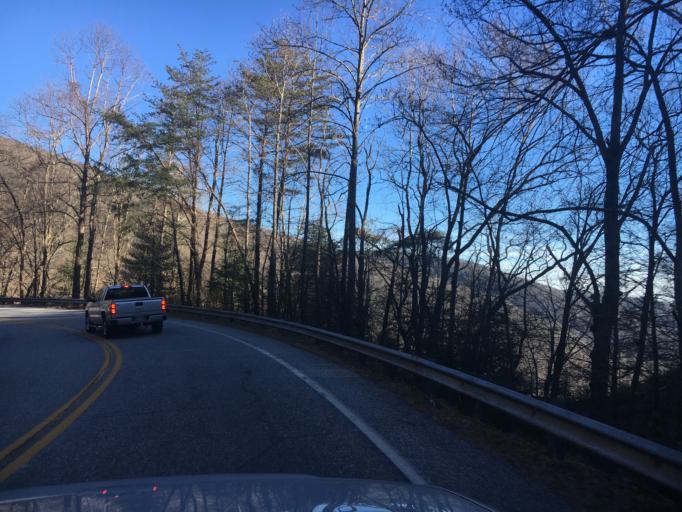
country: US
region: Georgia
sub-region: Union County
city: Blairsville
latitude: 34.7309
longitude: -83.9216
